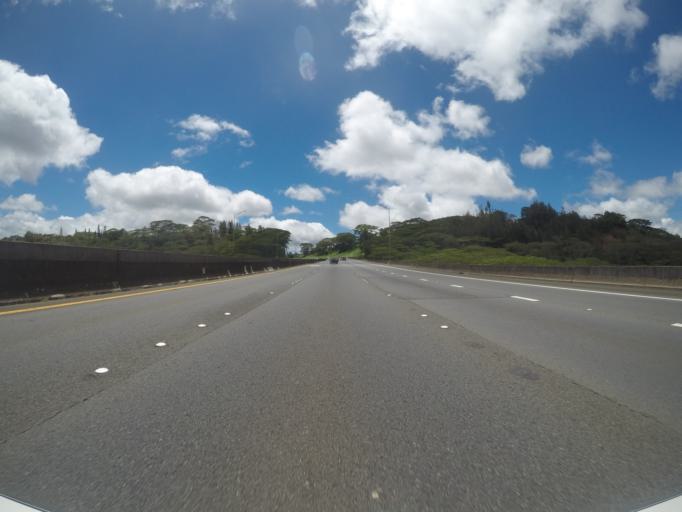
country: US
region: Hawaii
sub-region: Honolulu County
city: Mililani Town
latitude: 21.4594
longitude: -157.9938
